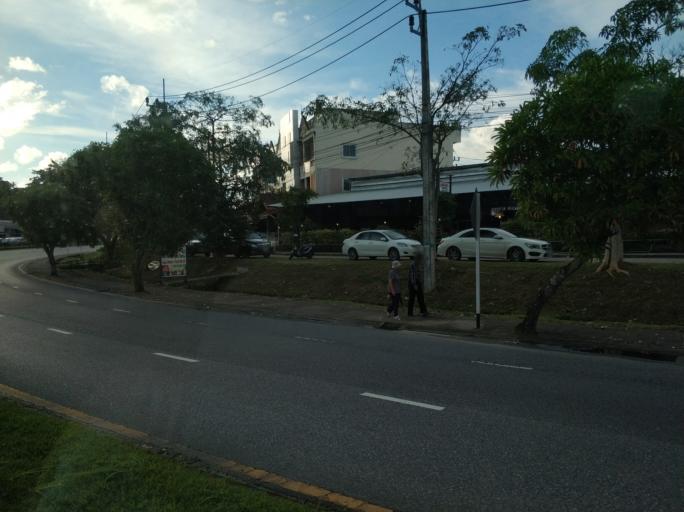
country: TH
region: Phuket
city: Kathu
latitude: 7.8991
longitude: 98.3526
